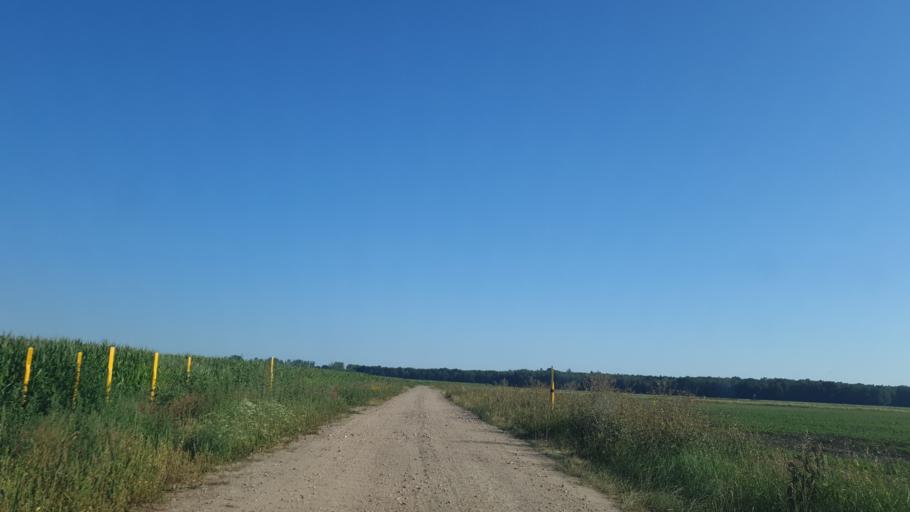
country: DE
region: Mecklenburg-Vorpommern
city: Torgelow
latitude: 53.6429
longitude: 13.9503
